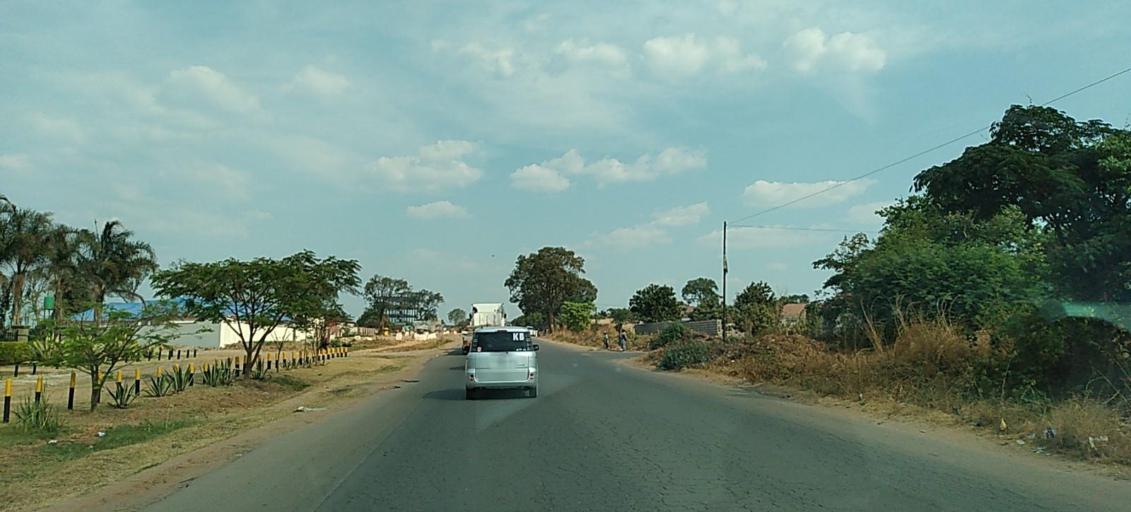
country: ZM
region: Copperbelt
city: Chililabombwe
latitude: -12.3608
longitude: 27.8494
